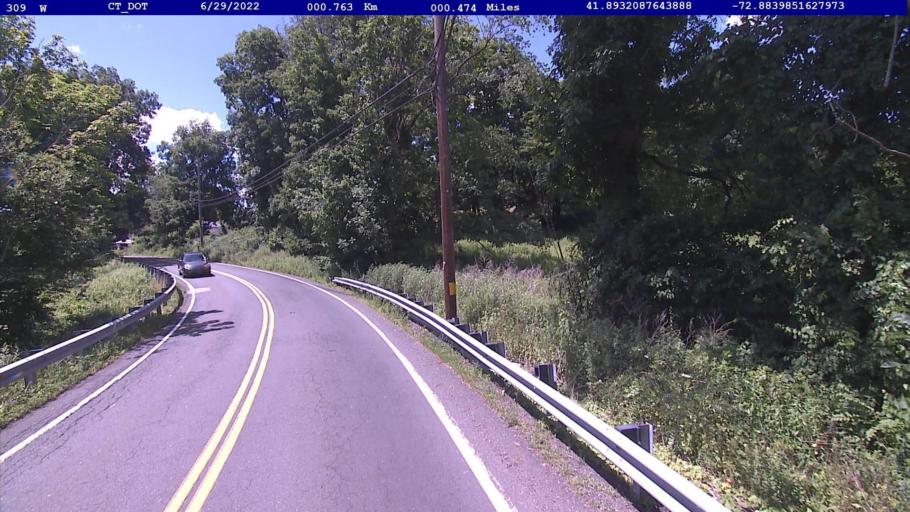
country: US
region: Connecticut
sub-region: Hartford County
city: West Simsbury
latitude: 41.8932
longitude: -72.8840
